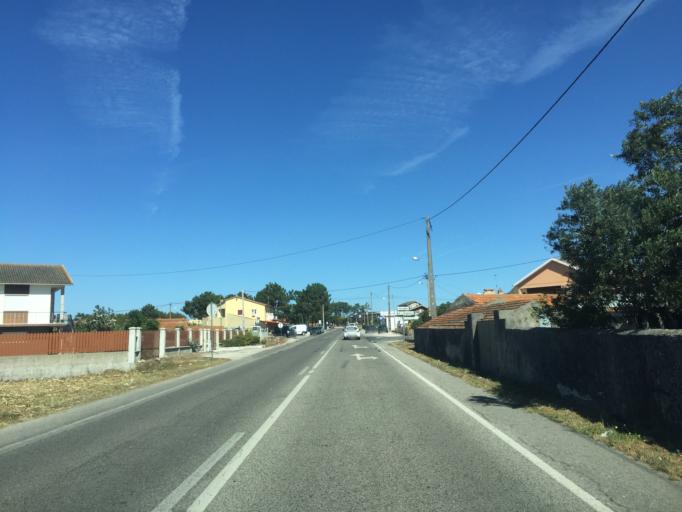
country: PT
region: Coimbra
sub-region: Figueira da Foz
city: Alhadas
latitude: 40.2550
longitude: -8.7814
